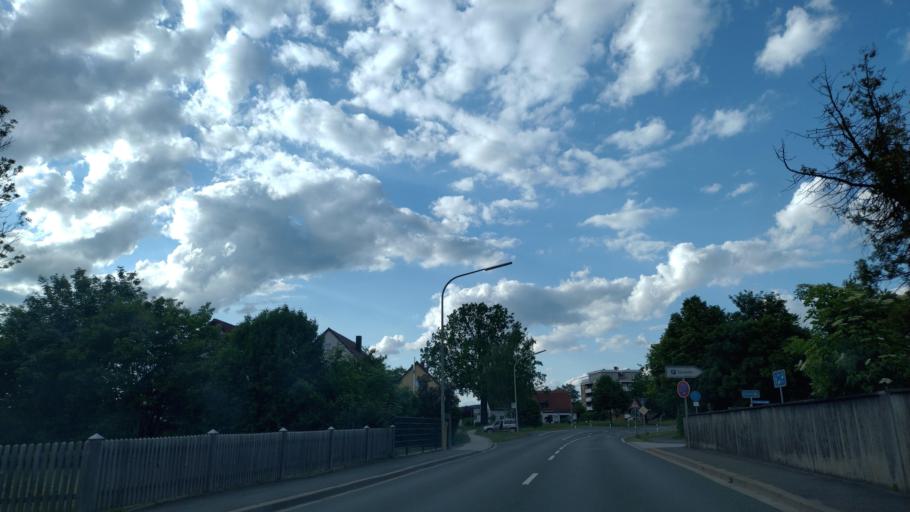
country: DE
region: Bavaria
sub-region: Upper Franconia
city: Bindlach
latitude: 49.9828
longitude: 11.6106
